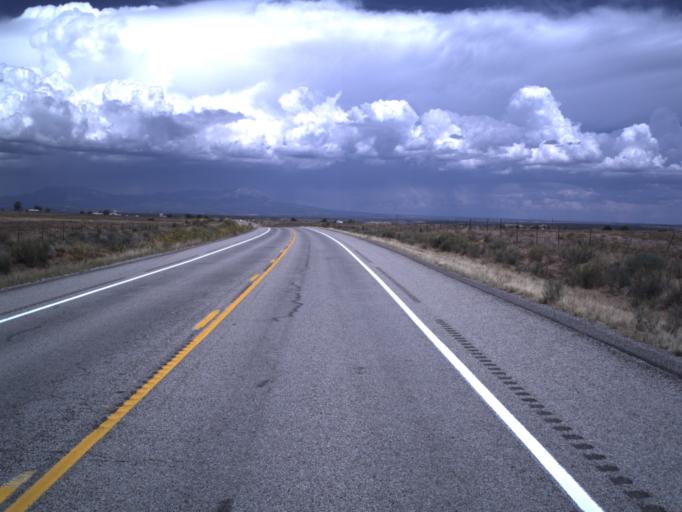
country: US
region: Utah
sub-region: San Juan County
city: Blanding
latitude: 37.4466
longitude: -109.4673
